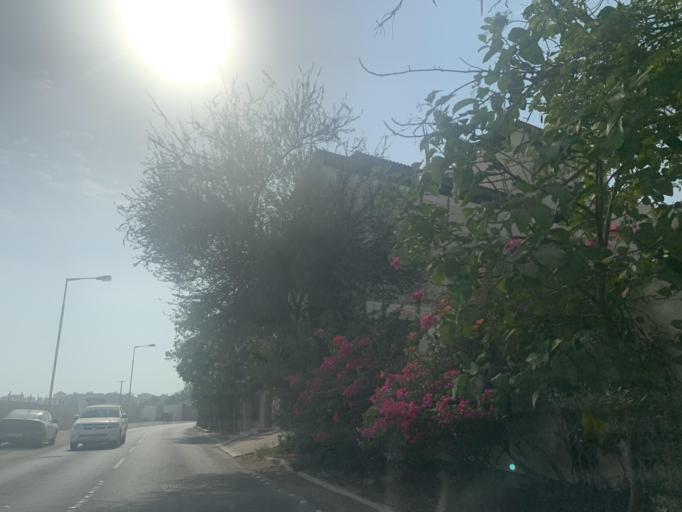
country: BH
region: Manama
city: Jidd Hafs
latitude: 26.2152
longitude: 50.4955
